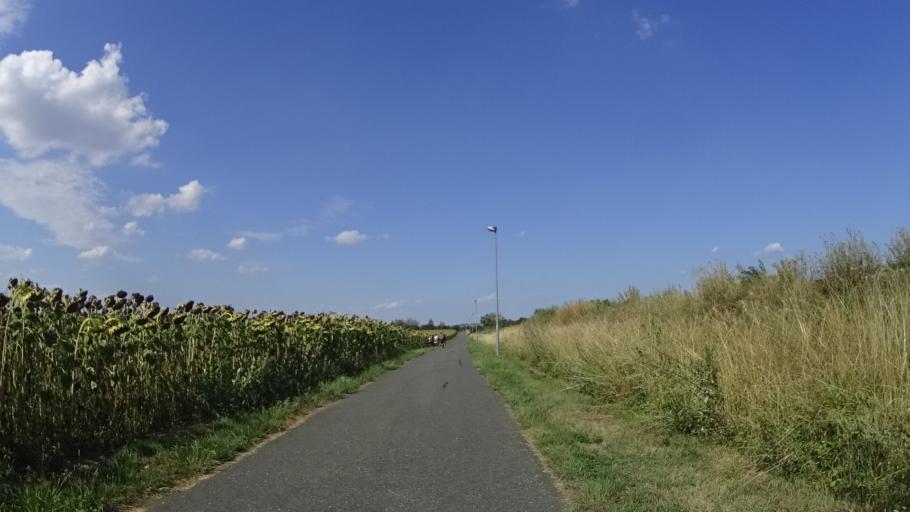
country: CZ
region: Zlin
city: Kunovice
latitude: 49.0262
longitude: 17.4533
